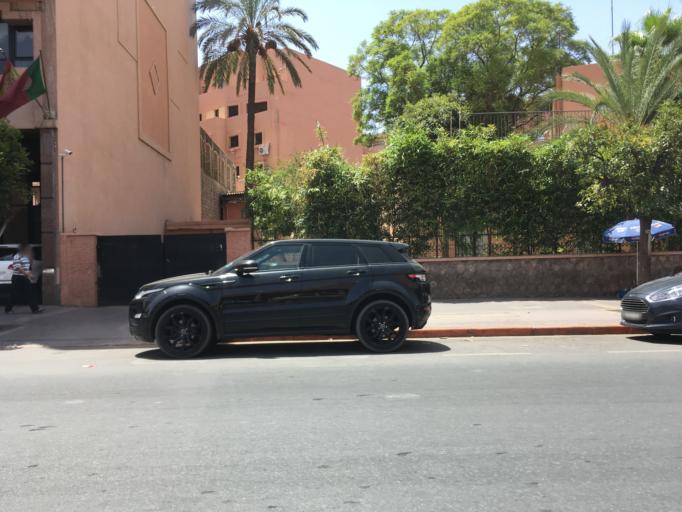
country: MA
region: Marrakech-Tensift-Al Haouz
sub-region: Marrakech
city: Marrakesh
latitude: 31.6355
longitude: -8.0136
